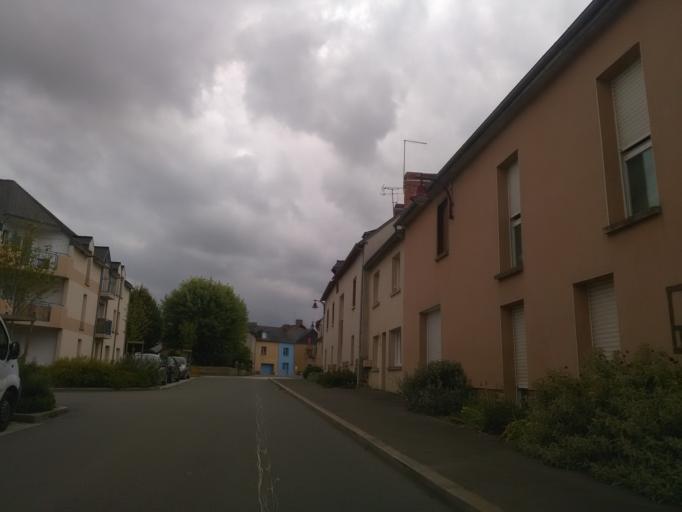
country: FR
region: Brittany
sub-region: Departement d'Ille-et-Vilaine
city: Vignoc
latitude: 48.2494
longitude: -1.7813
